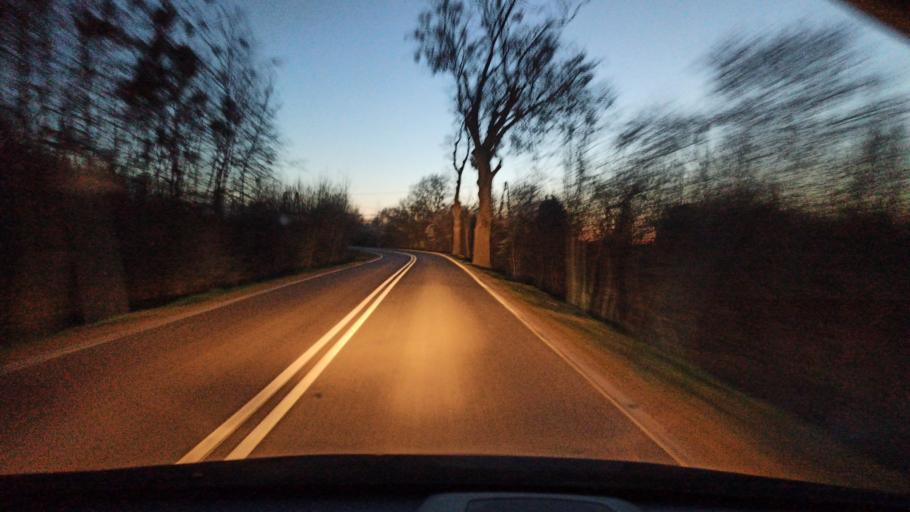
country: PL
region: Warmian-Masurian Voivodeship
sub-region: Powiat elblaski
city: Gronowo Gorne
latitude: 54.1679
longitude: 19.4857
